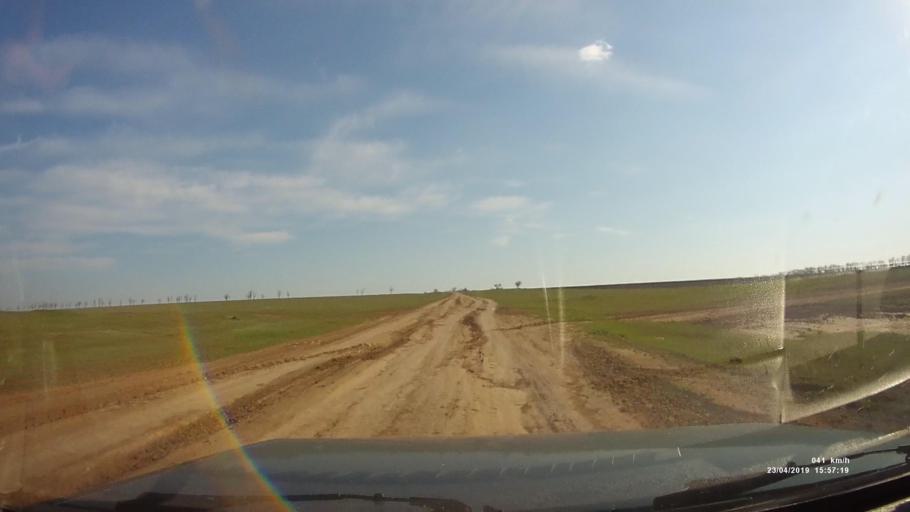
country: RU
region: Rostov
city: Remontnoye
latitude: 46.5325
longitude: 43.1101
